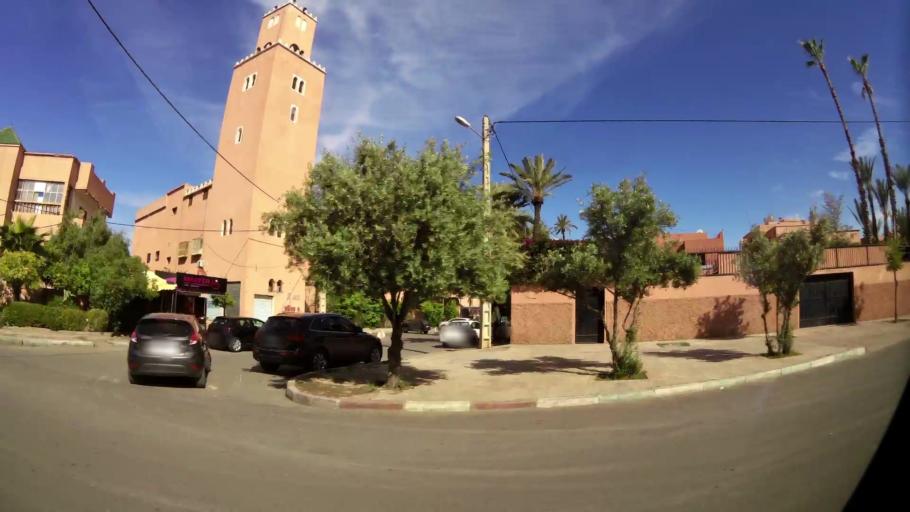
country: MA
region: Marrakech-Tensift-Al Haouz
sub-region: Marrakech
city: Marrakesh
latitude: 31.6523
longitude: -8.0105
